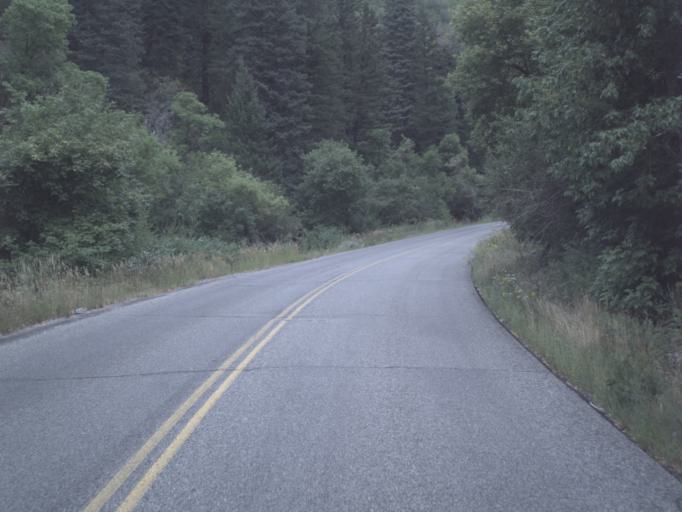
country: US
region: Utah
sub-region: Utah County
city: Orem
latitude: 40.3723
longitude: -111.5688
